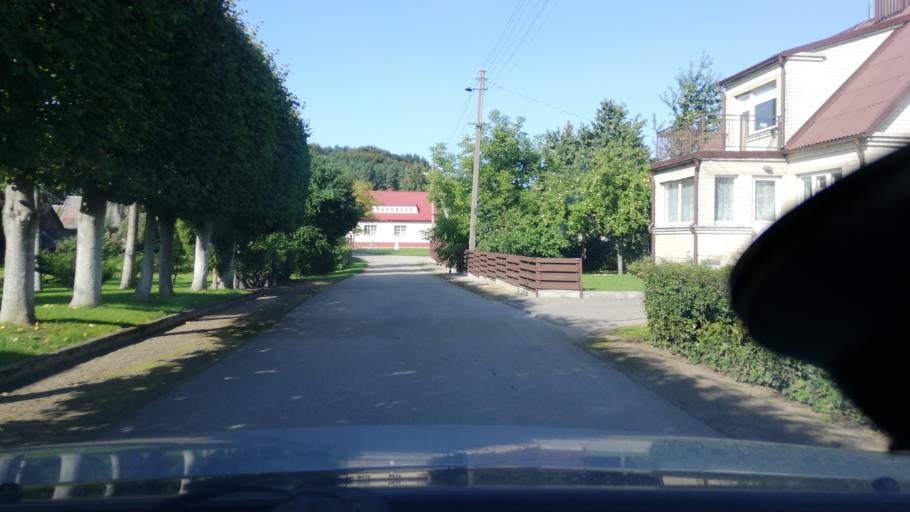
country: LT
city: Salantai
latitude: 55.9234
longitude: 21.4732
